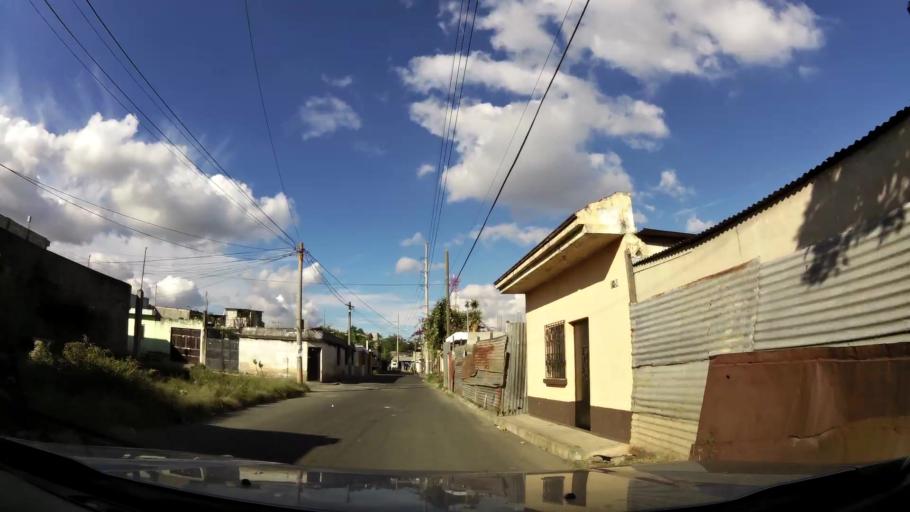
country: GT
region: Guatemala
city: Villa Nueva
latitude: 14.5249
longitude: -90.5788
